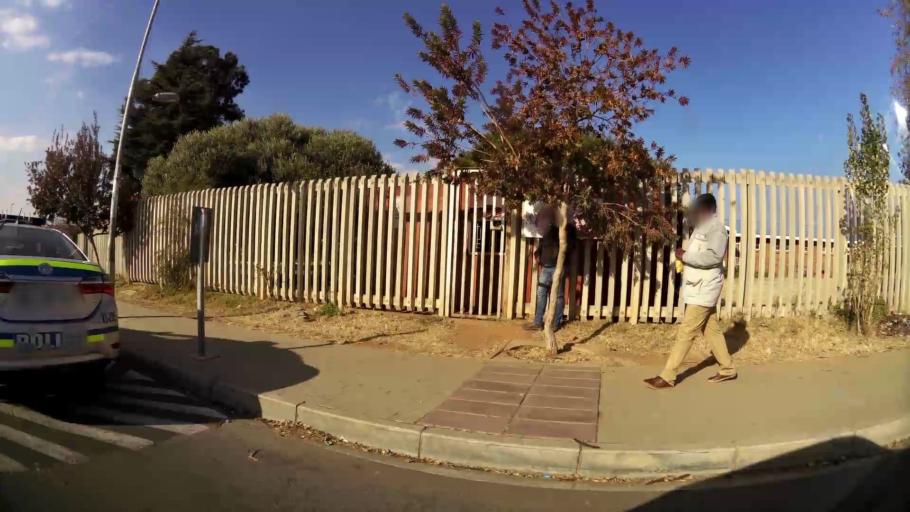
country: ZA
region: Gauteng
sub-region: City of Johannesburg Metropolitan Municipality
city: Soweto
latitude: -26.2579
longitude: 27.9154
